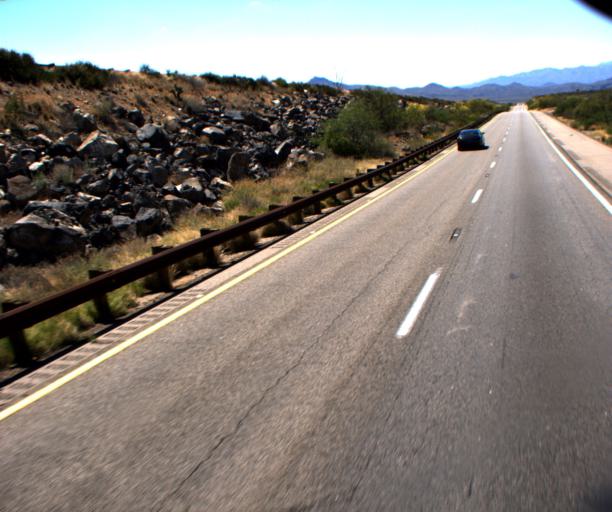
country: US
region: Arizona
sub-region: Yavapai County
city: Bagdad
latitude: 34.4873
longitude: -113.3753
